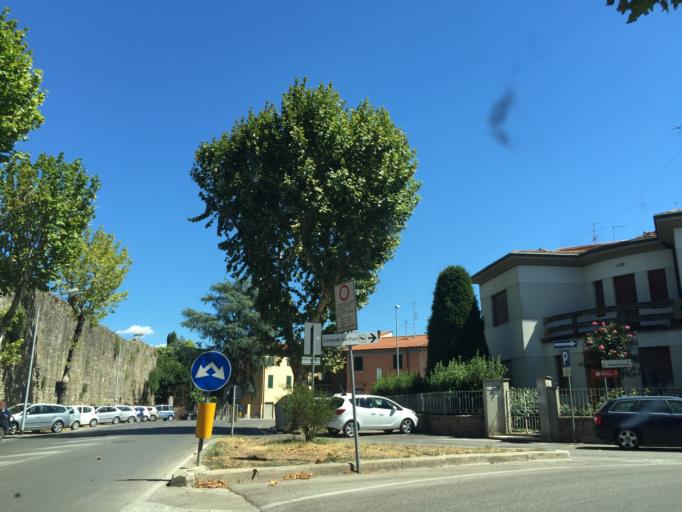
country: IT
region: Tuscany
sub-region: Provincia di Pistoia
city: Pistoia
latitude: 43.9384
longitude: 10.9224
